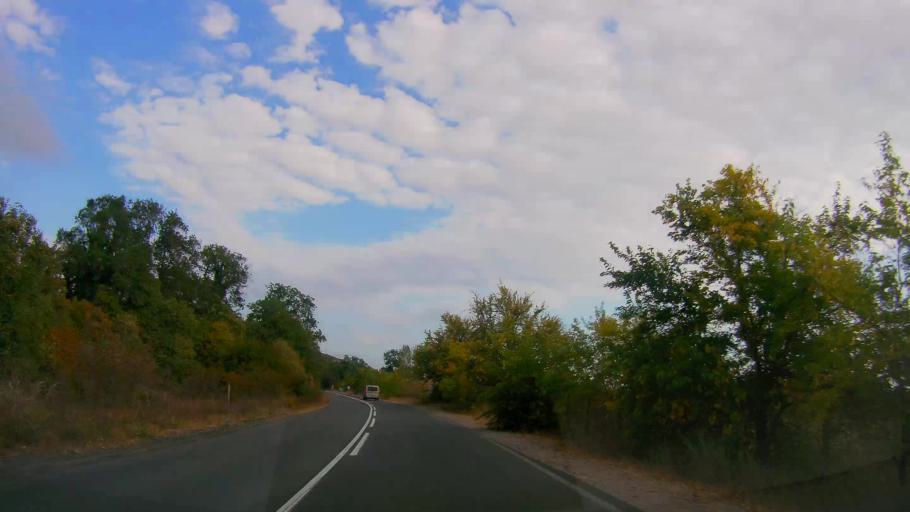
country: BG
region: Burgas
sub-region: Obshtina Primorsko
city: Primorsko
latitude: 42.3269
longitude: 27.7307
